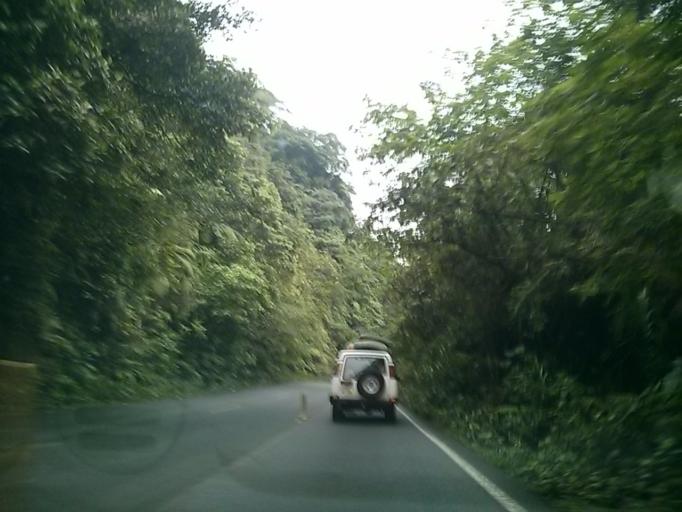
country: CR
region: San Jose
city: Dulce Nombre de Jesus
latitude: 10.1415
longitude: -83.9733
